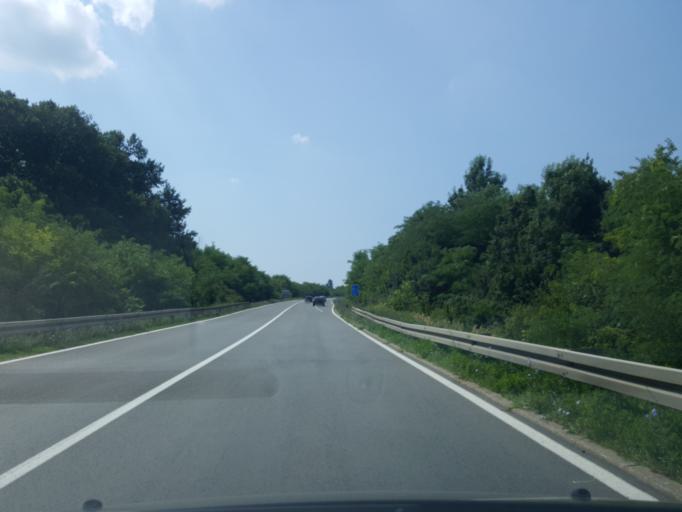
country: RS
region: Central Serbia
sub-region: Belgrade
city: Sopot
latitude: 44.5571
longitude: 20.6671
